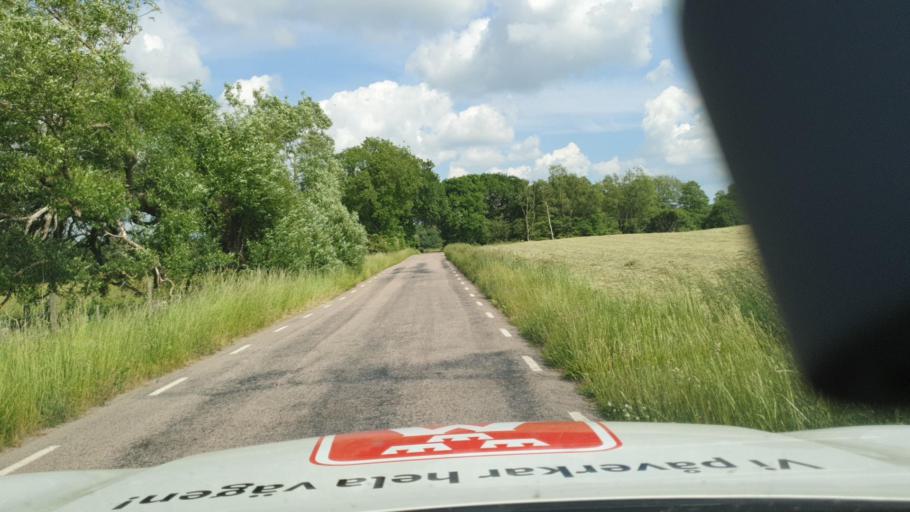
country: SE
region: Skane
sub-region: Svedala Kommun
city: Svedala
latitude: 55.5339
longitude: 13.2528
